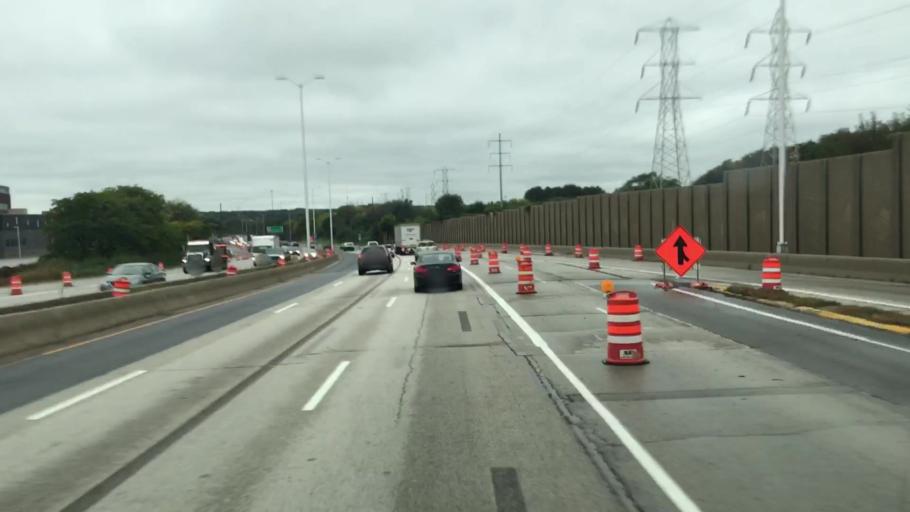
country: US
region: Wisconsin
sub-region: Milwaukee County
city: Greenfield
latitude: 42.9623
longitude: -88.0205
